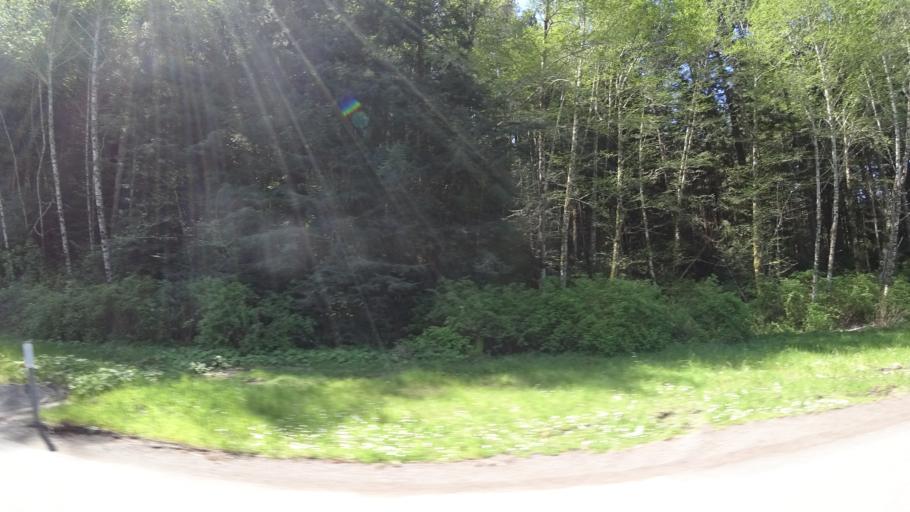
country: US
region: California
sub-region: Humboldt County
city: Westhaven-Moonstone
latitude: 41.4062
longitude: -124.0001
